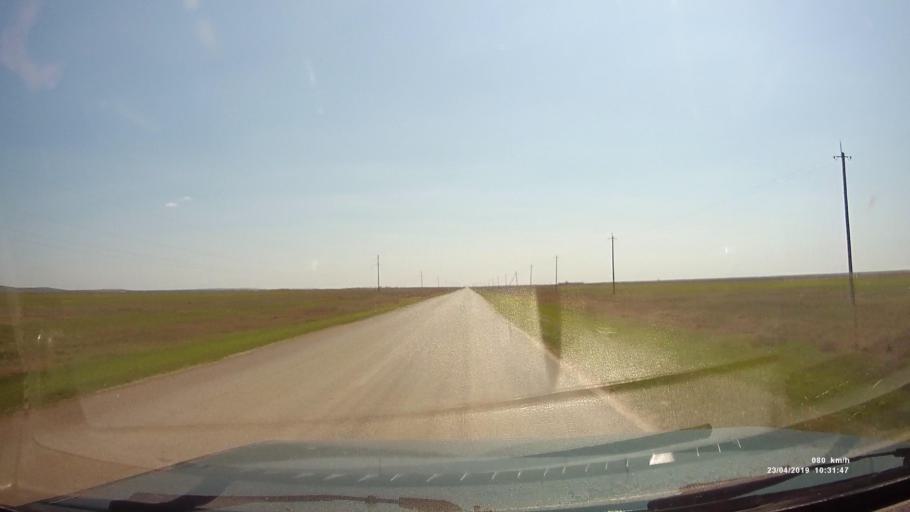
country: RU
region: Kalmykiya
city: Yashalta
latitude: 46.5841
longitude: 42.5669
